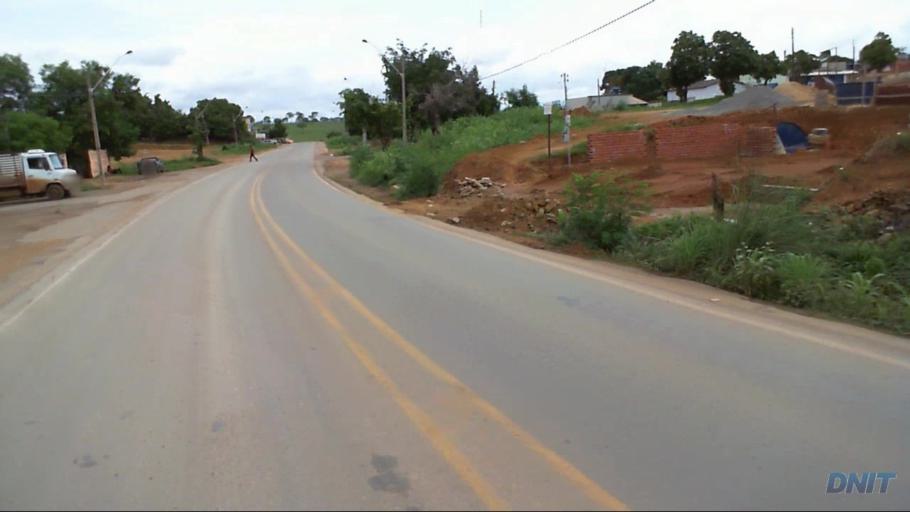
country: BR
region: Goias
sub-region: Padre Bernardo
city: Padre Bernardo
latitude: -15.1665
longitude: -48.2913
